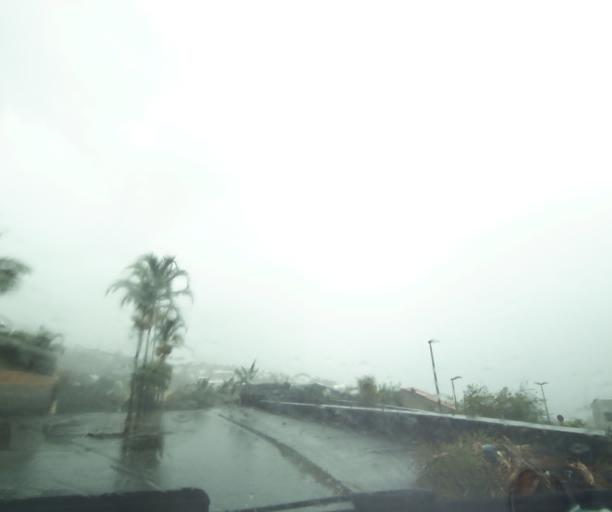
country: RE
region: Reunion
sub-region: Reunion
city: Saint-Paul
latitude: -20.9907
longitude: 55.3279
